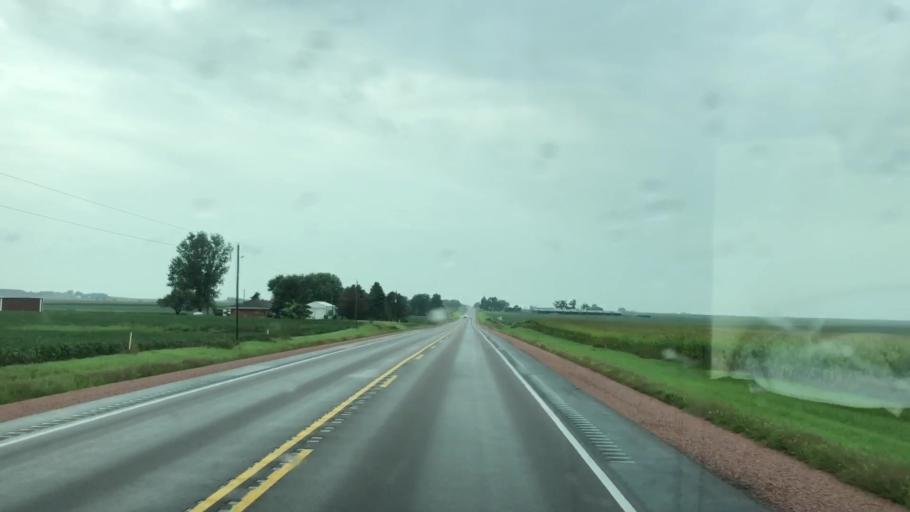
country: US
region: Iowa
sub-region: O'Brien County
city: Sheldon
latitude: 43.1862
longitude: -95.7677
